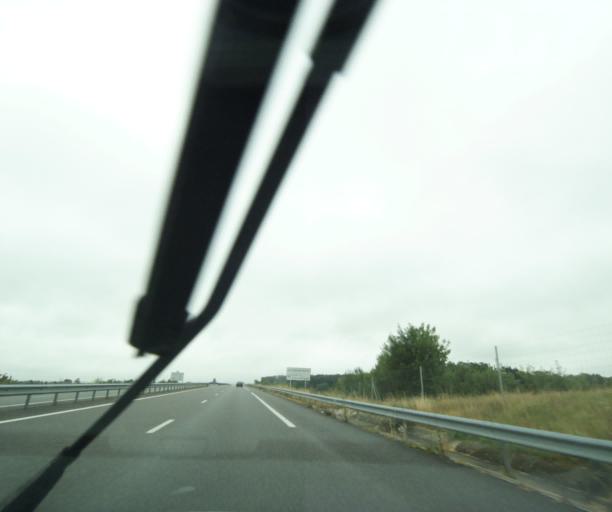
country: FR
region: Midi-Pyrenees
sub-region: Departement du Tarn
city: Le Garric
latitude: 44.0231
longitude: 2.1852
